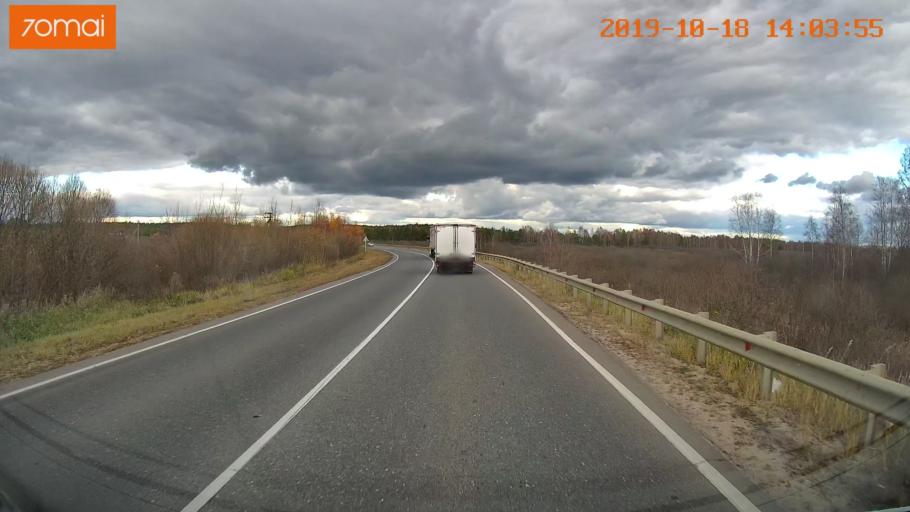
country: RU
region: Rjazan
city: Spas-Klepiki
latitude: 55.1207
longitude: 40.1330
